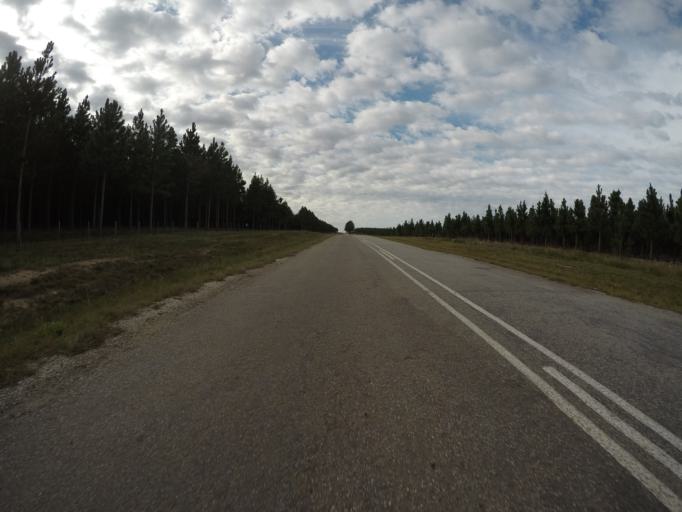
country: ZA
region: Eastern Cape
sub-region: Cacadu District Municipality
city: Kareedouw
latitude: -34.0266
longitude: 24.3705
